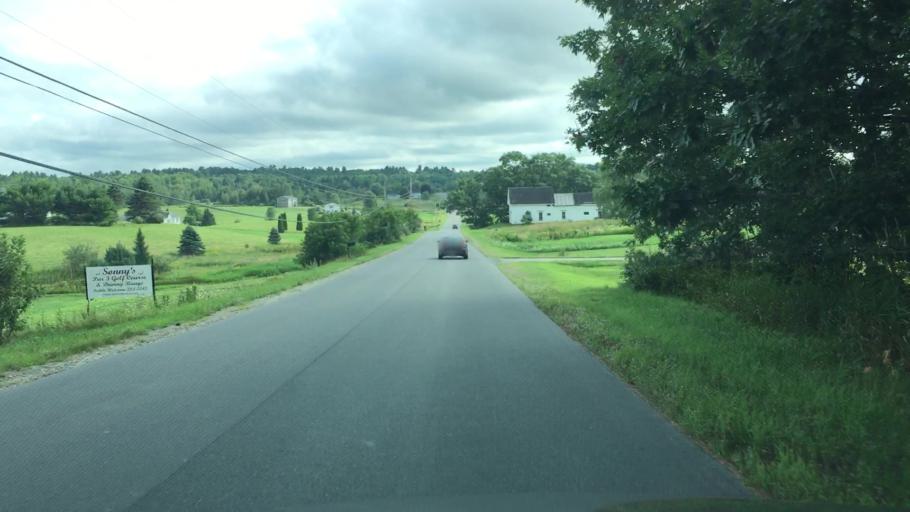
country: US
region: Maine
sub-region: Waldo County
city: Winterport
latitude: 44.6777
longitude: -68.8678
